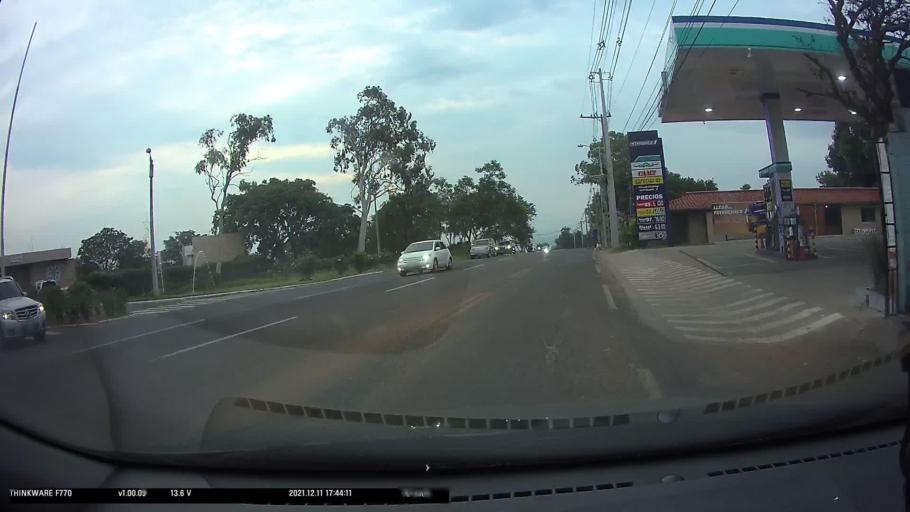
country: PY
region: Cordillera
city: San Bernardino
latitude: -25.2969
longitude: -57.2693
